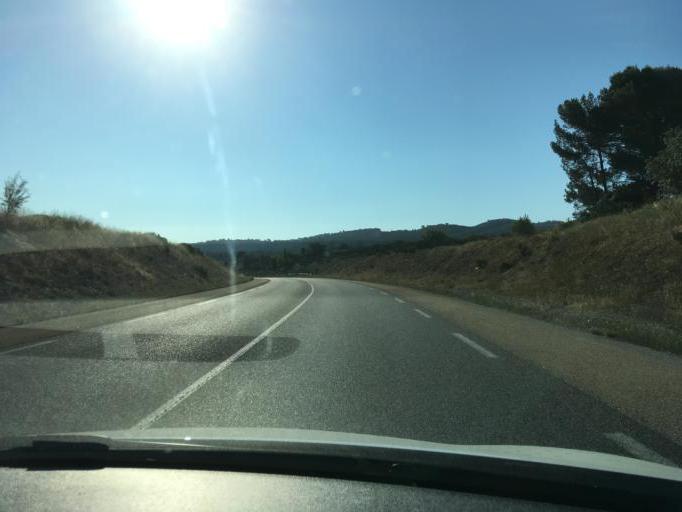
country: FR
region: Provence-Alpes-Cote d'Azur
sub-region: Departement des Bouches-du-Rhone
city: Charleval
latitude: 43.7115
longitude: 5.2290
